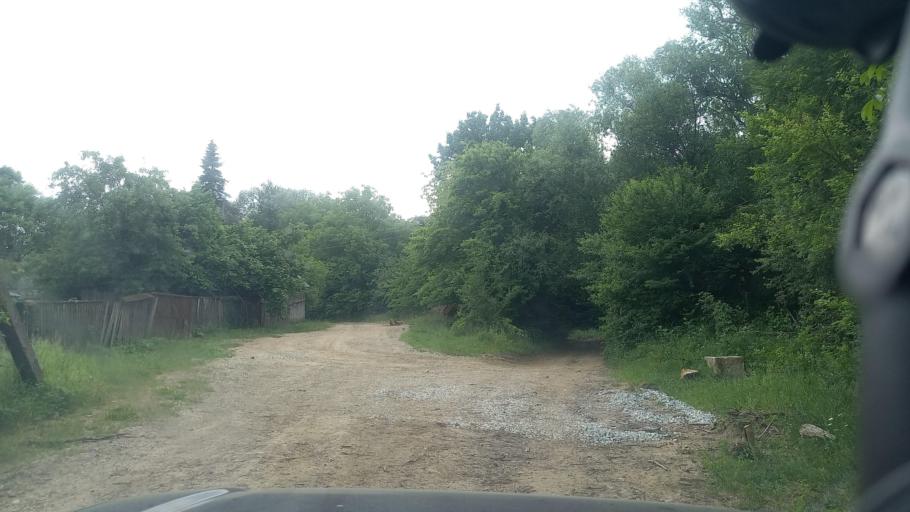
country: RU
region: Krasnodarskiy
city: Goryachiy Klyuch
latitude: 44.6099
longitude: 39.0340
